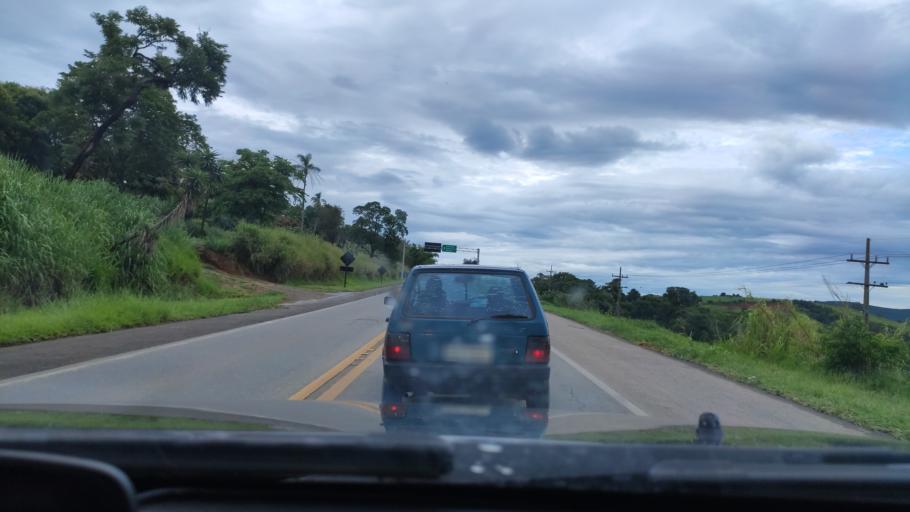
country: BR
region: Sao Paulo
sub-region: Braganca Paulista
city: Braganca Paulista
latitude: -22.9002
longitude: -46.5426
